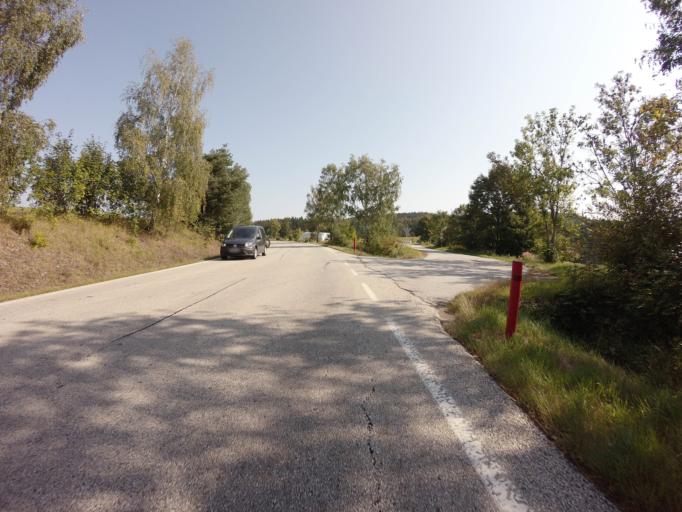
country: CZ
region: Jihocesky
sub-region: Okres Cesky Krumlov
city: Vyssi Brod
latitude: 48.6000
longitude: 14.3215
